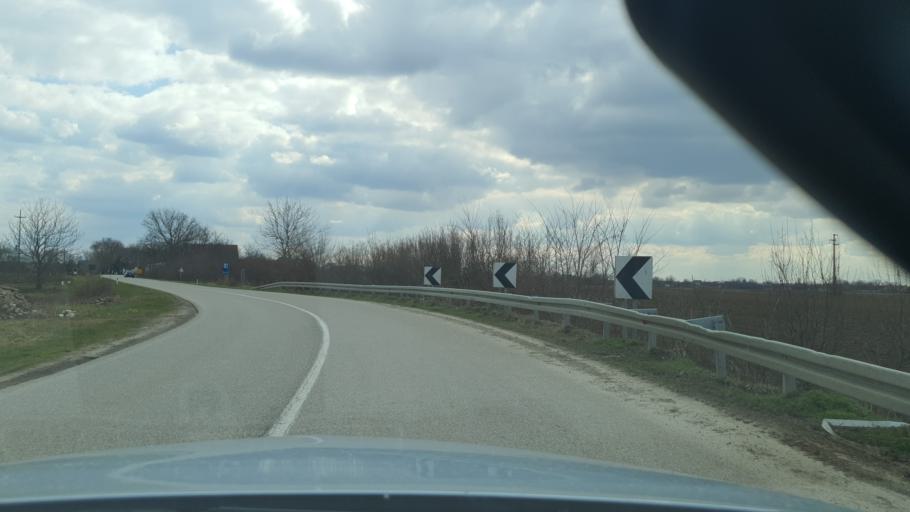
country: RS
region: Autonomna Pokrajina Vojvodina
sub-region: Juznobacki Okrug
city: Bac
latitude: 45.4222
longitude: 19.3089
